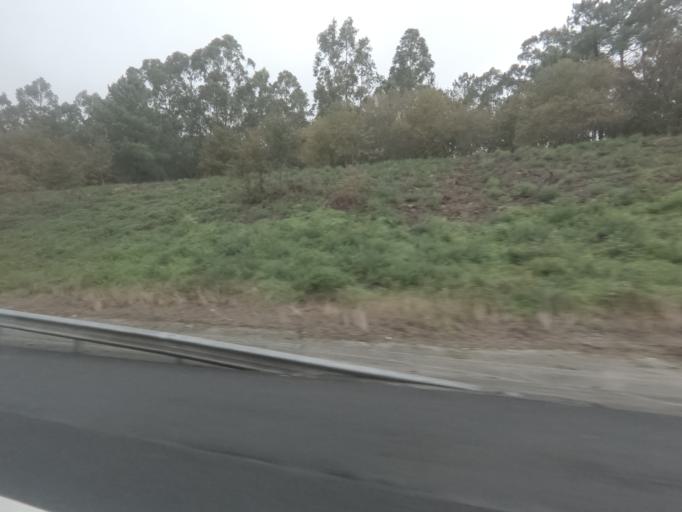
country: ES
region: Galicia
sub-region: Provincia de Pontevedra
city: Redondela
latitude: 42.2391
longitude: -8.6571
